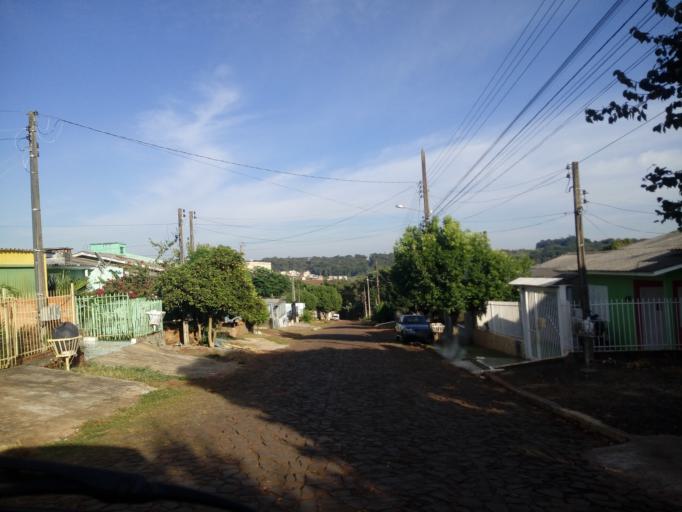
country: BR
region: Santa Catarina
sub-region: Chapeco
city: Chapeco
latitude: -27.0876
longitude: -52.6773
